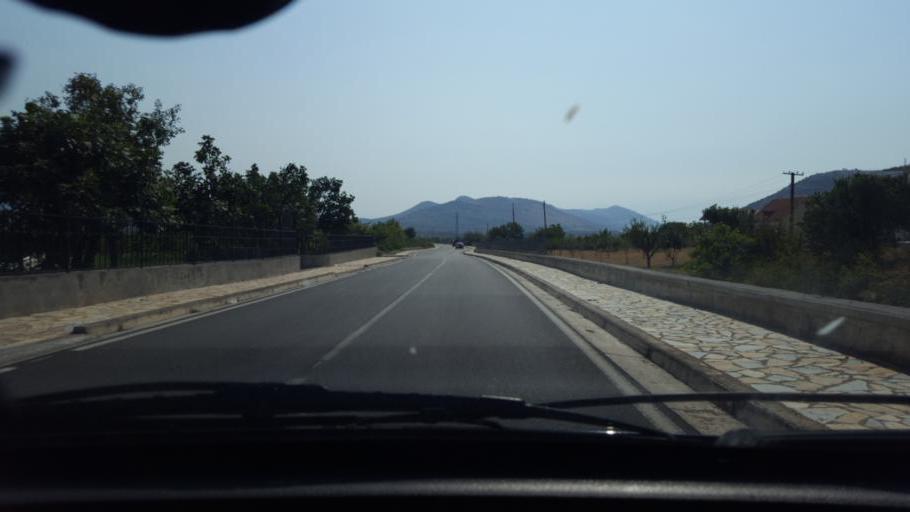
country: AL
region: Shkoder
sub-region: Rrethi i Malesia e Madhe
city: Hot
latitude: 42.3503
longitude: 19.4411
